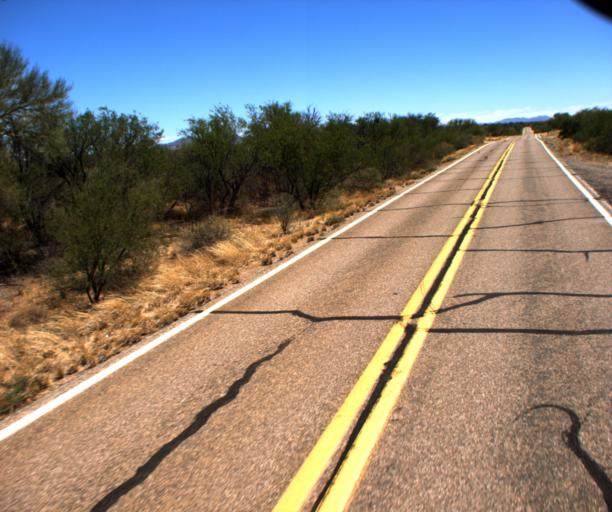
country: US
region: Arizona
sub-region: Pima County
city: Three Points
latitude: 31.9285
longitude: -111.3909
